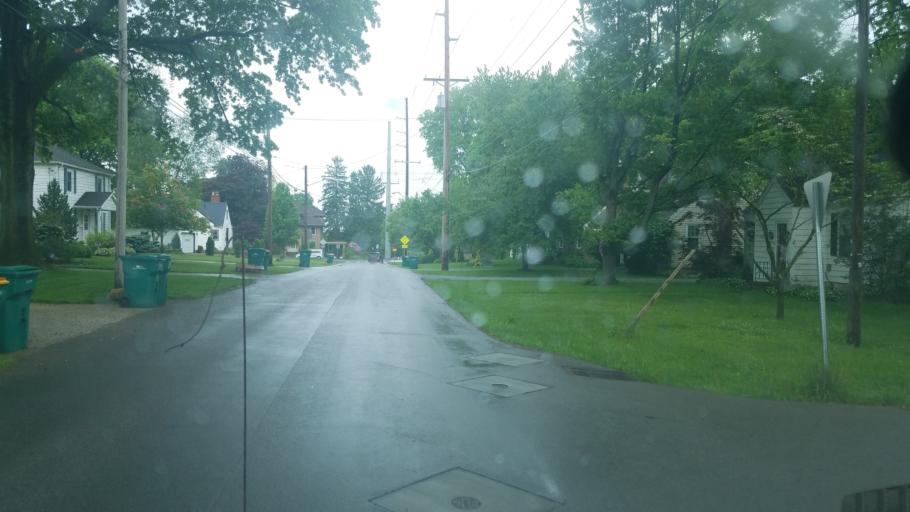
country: US
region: Ohio
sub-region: Wayne County
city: Wooster
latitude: 40.8246
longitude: -81.9372
